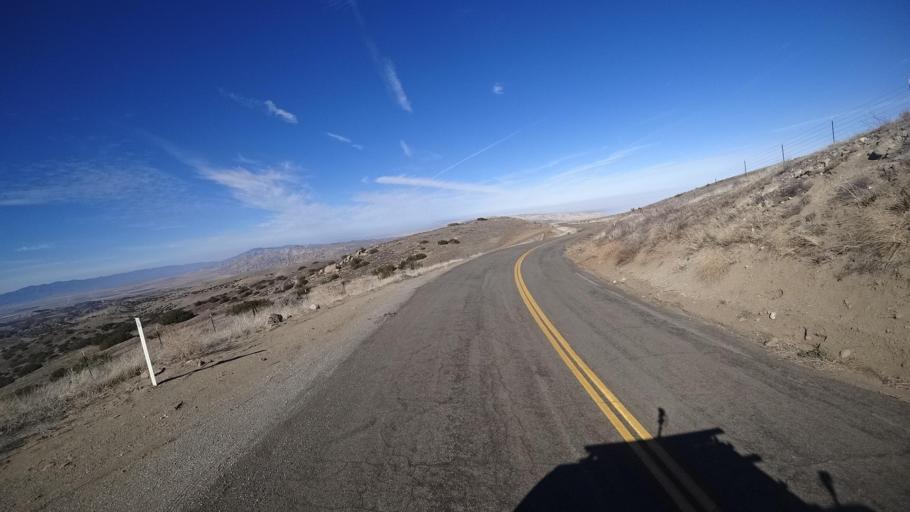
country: US
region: California
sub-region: Kern County
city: Maricopa
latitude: 34.9166
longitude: -119.4116
